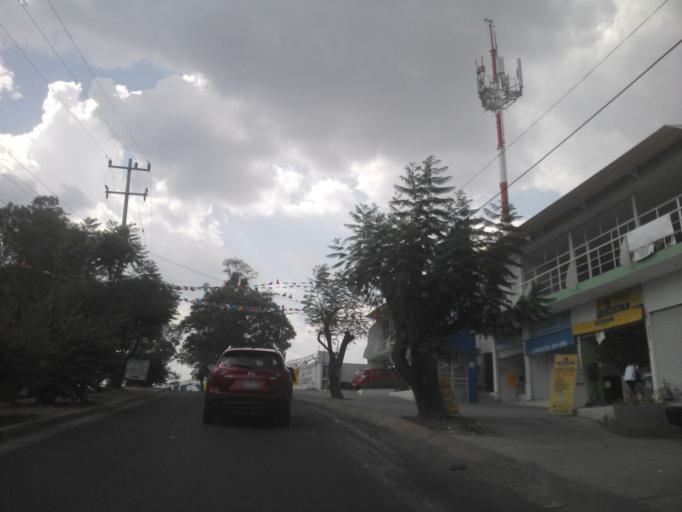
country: MX
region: Jalisco
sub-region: San Pedro Tlaquepaque
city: Paseo del Prado
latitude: 20.6117
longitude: -103.3946
